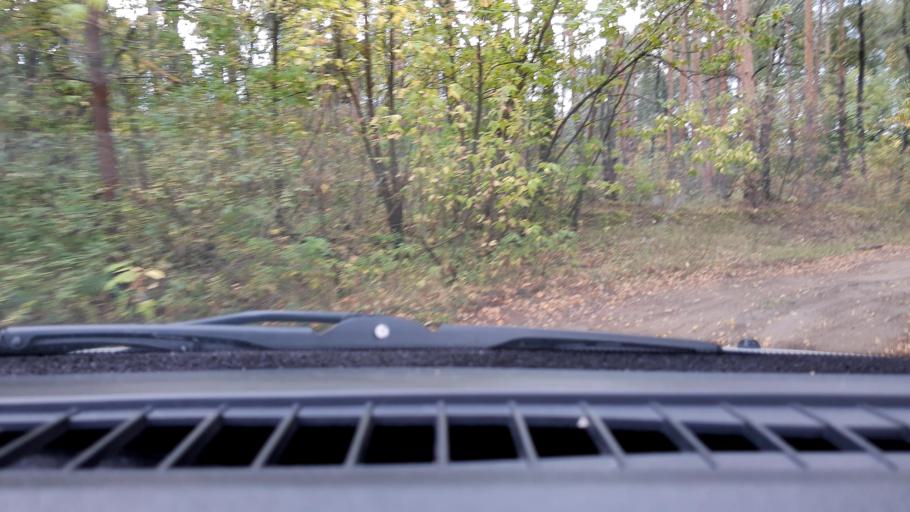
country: RU
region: Nizjnij Novgorod
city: Gorbatovka
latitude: 56.3090
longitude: 43.7179
